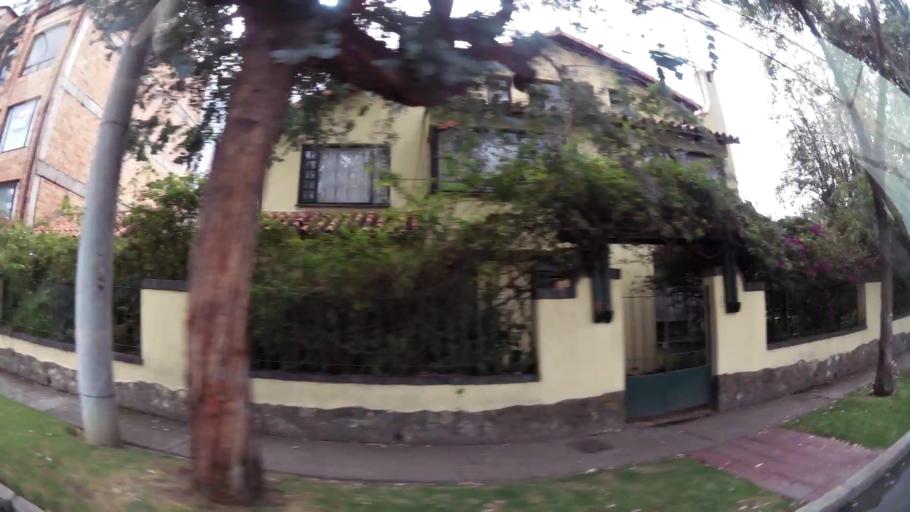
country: CO
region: Bogota D.C.
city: Barrio San Luis
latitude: 4.6948
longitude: -74.0593
